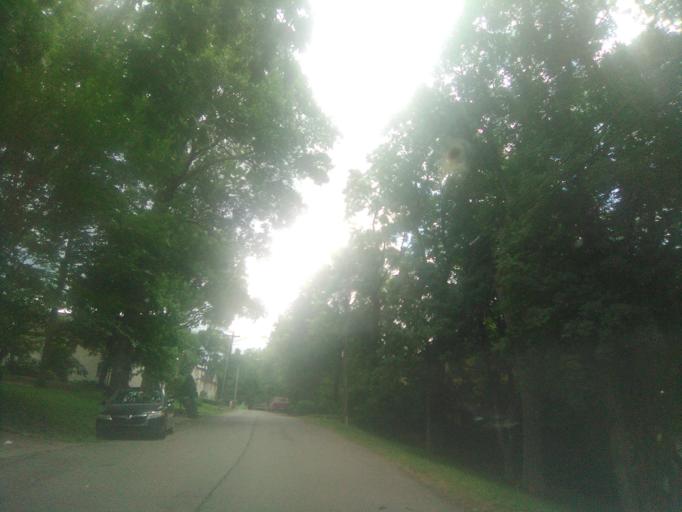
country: US
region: Tennessee
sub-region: Davidson County
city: Belle Meade
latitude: 36.1130
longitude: -86.8396
